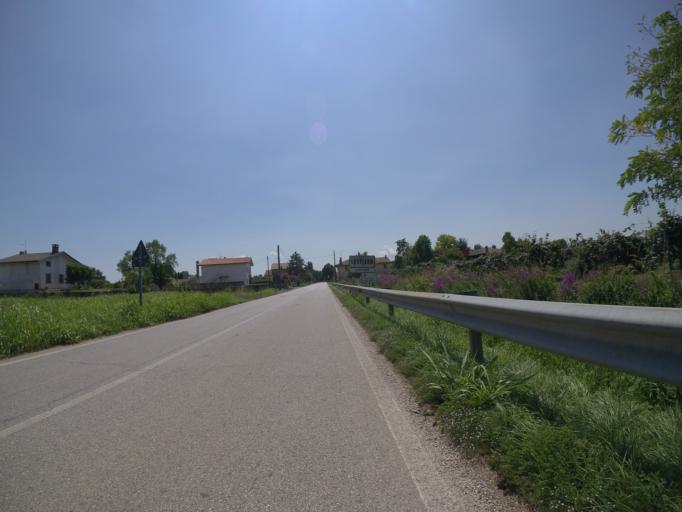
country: IT
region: Friuli Venezia Giulia
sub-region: Provincia di Udine
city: Lestizza
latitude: 45.9617
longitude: 13.1399
